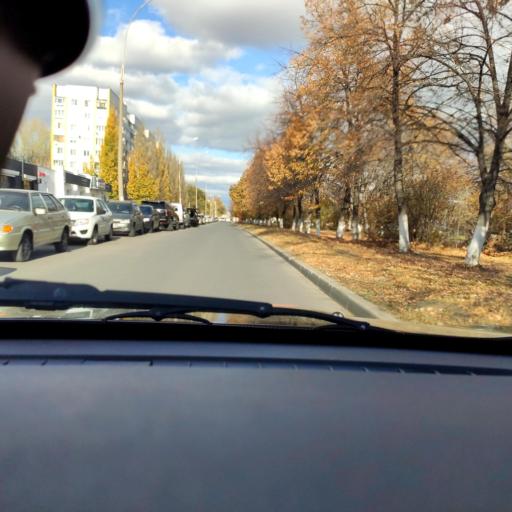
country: RU
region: Samara
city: Tol'yatti
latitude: 53.5311
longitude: 49.3127
